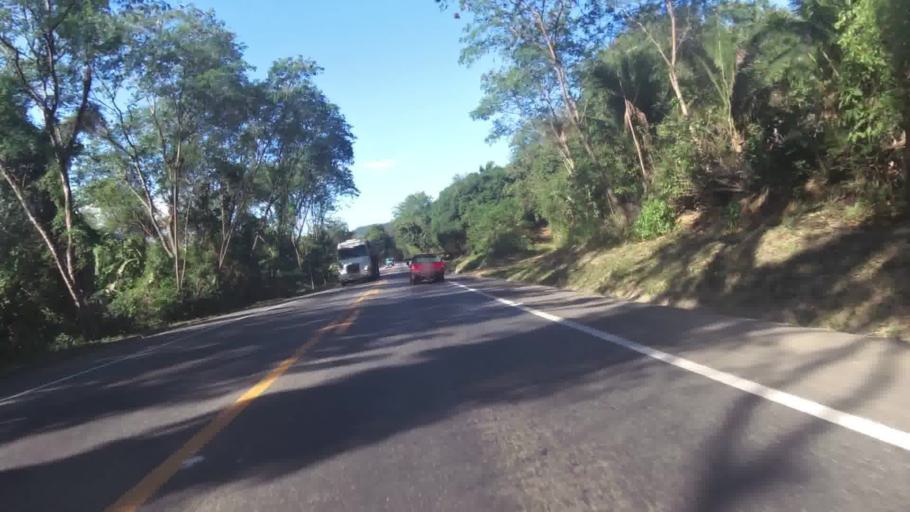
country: BR
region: Espirito Santo
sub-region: Iconha
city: Iconha
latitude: -20.7709
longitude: -40.7755
